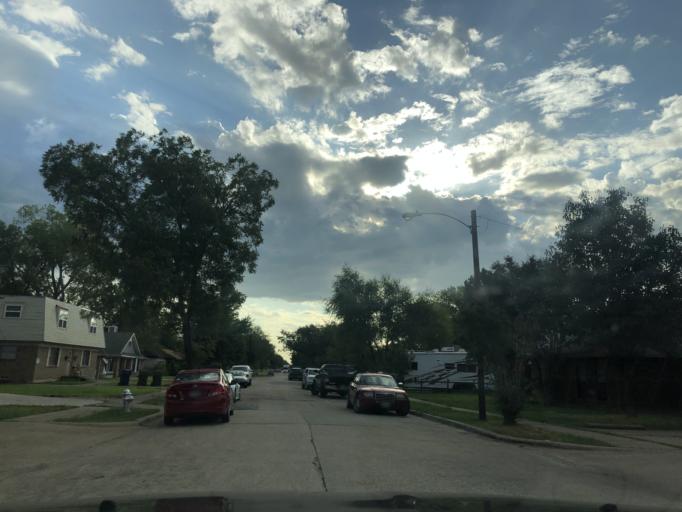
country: US
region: Texas
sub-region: Dallas County
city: Garland
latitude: 32.8762
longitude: -96.6546
